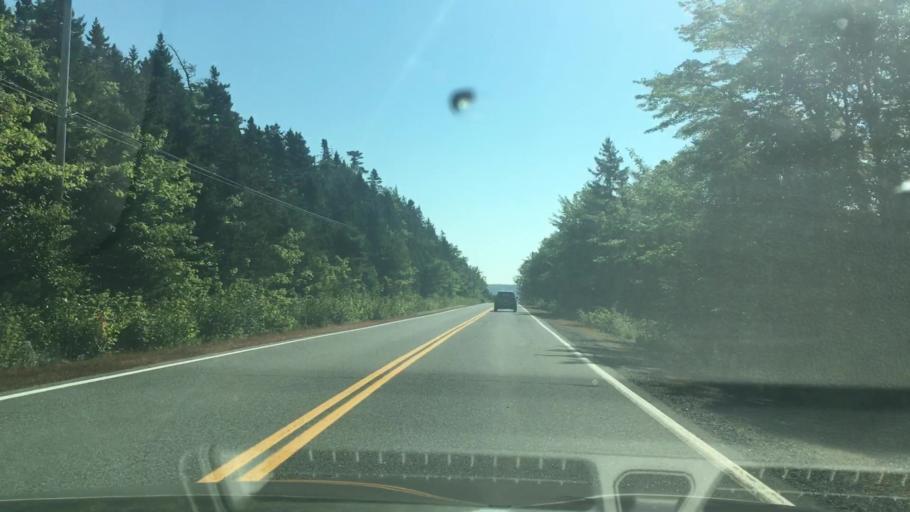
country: CA
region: Nova Scotia
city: Cole Harbour
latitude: 44.8163
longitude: -62.8805
